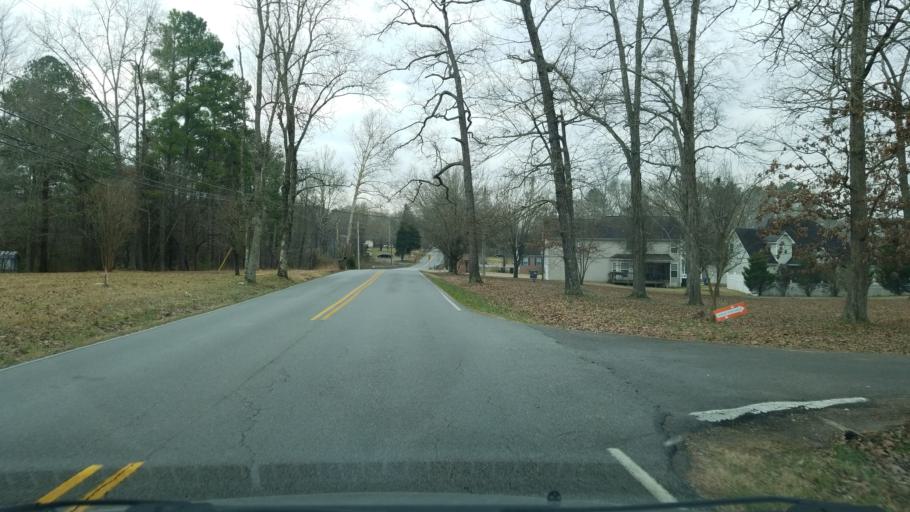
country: US
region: Georgia
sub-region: Catoosa County
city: Indian Springs
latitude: 34.9631
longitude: -85.1605
